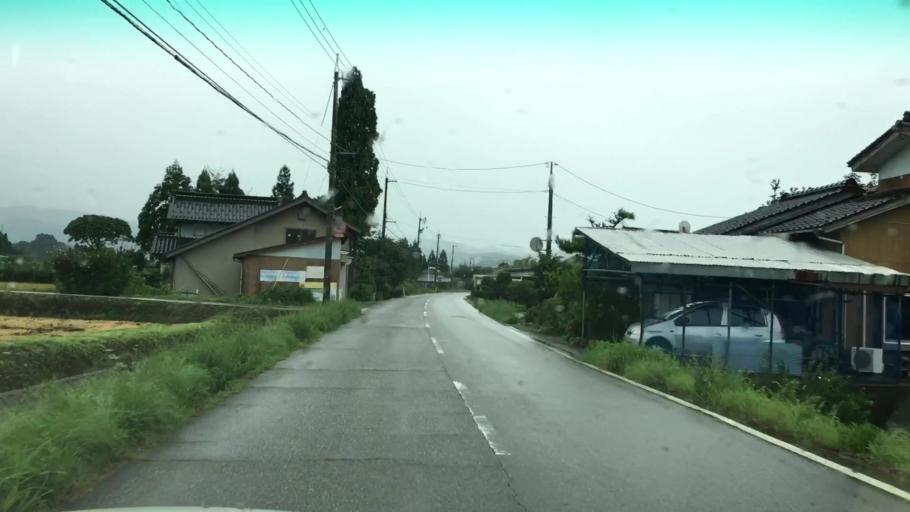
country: JP
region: Toyama
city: Kamiichi
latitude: 36.6206
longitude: 137.3231
